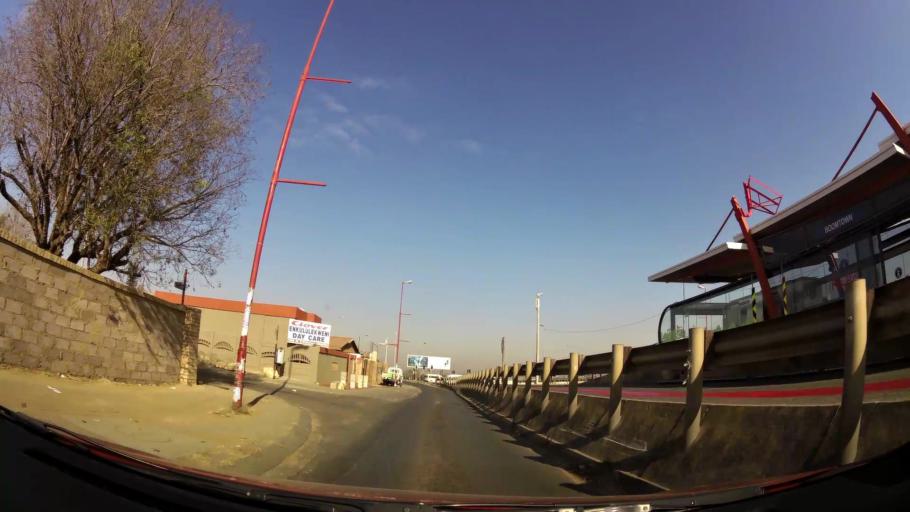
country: ZA
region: Gauteng
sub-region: City of Johannesburg Metropolitan Municipality
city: Soweto
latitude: -26.2424
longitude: 27.9151
